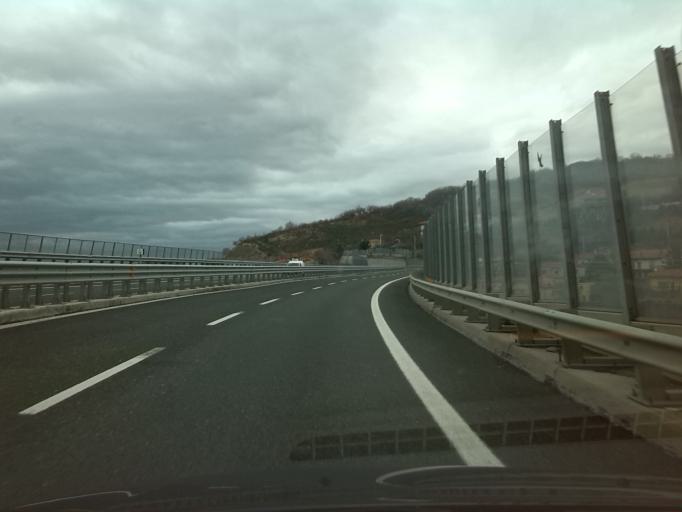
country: IT
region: Friuli Venezia Giulia
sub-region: Provincia di Trieste
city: Domio
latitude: 45.6306
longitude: 13.8191
